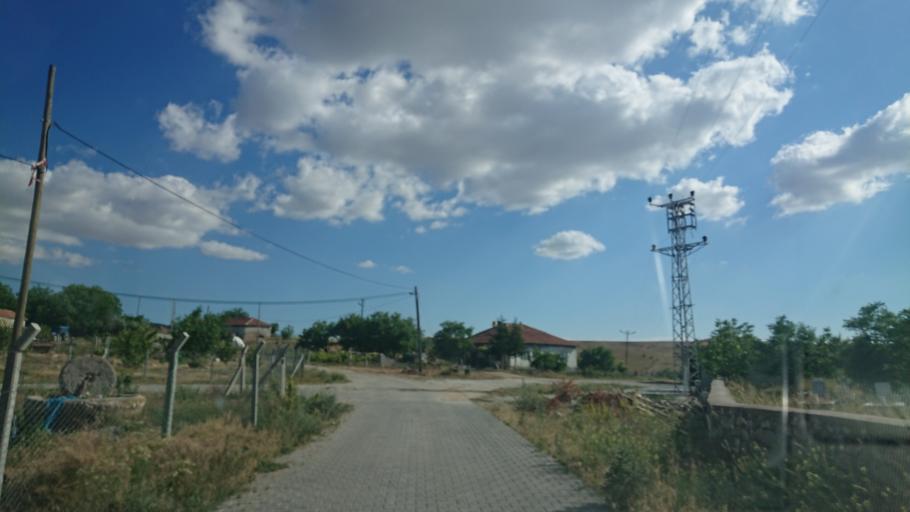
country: TR
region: Aksaray
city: Agacoren
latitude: 38.7529
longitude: 33.8849
